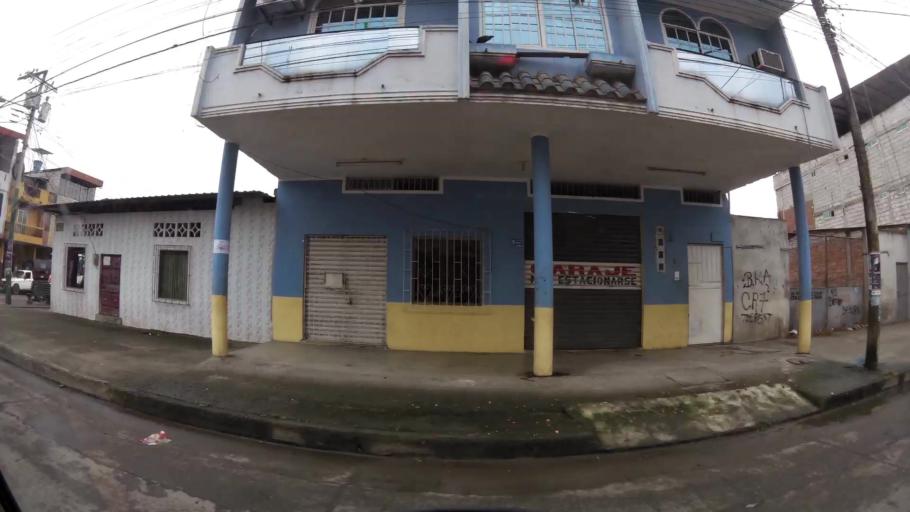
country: EC
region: El Oro
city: Pasaje
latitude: -3.3256
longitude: -79.8115
